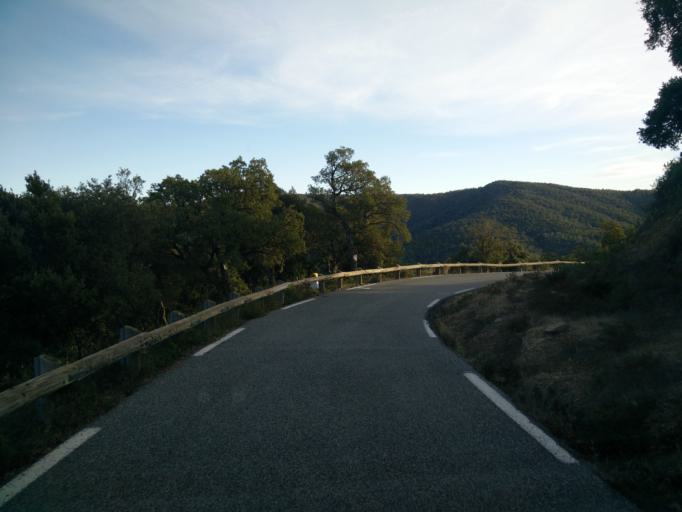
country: FR
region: Provence-Alpes-Cote d'Azur
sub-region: Departement du Var
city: Bormes-les-Mimosas
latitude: 43.1857
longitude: 6.3405
